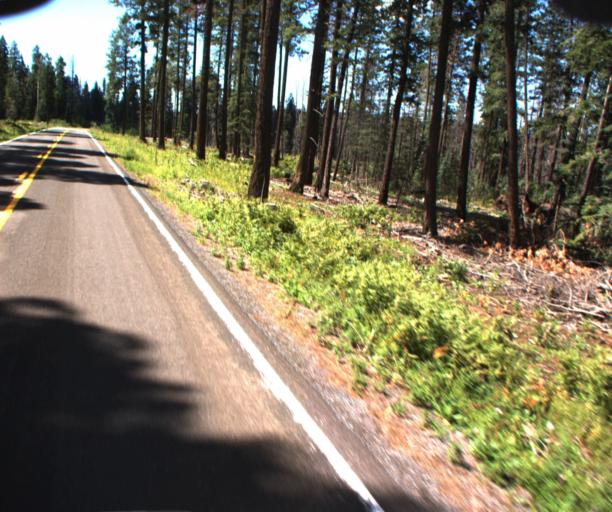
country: US
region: Arizona
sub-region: Apache County
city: Eagar
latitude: 33.6186
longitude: -109.3272
